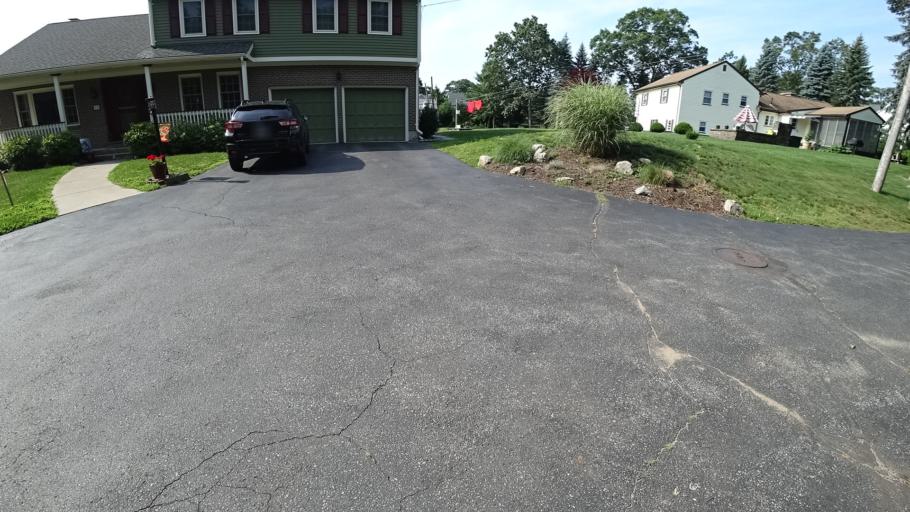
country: US
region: Massachusetts
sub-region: Norfolk County
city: Dedham
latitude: 42.2379
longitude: -71.1694
